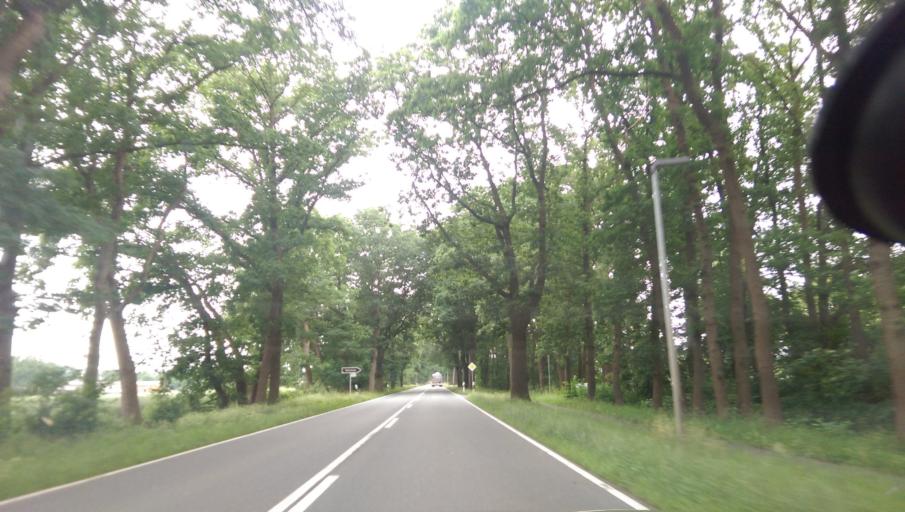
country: DE
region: Lower Saxony
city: Rotenburg
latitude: 53.0919
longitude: 9.4130
